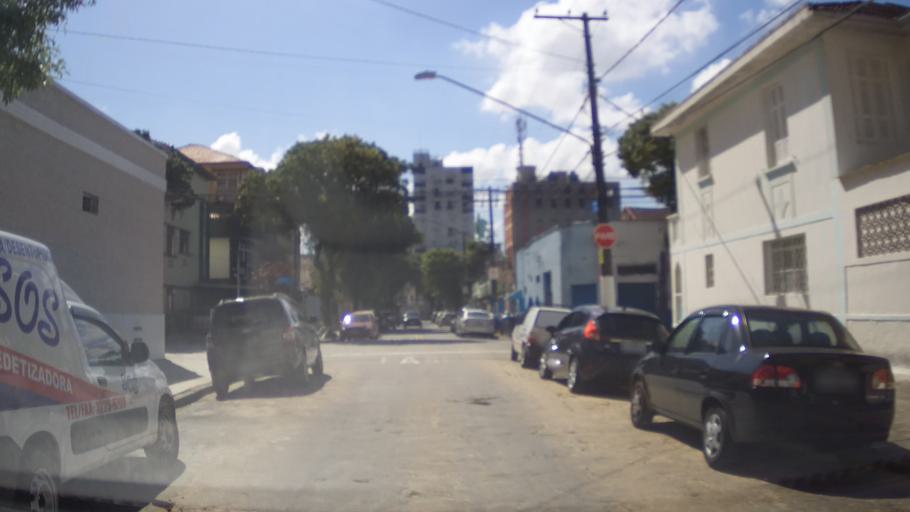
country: BR
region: Sao Paulo
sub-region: Santos
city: Santos
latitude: -23.9598
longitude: -46.3465
